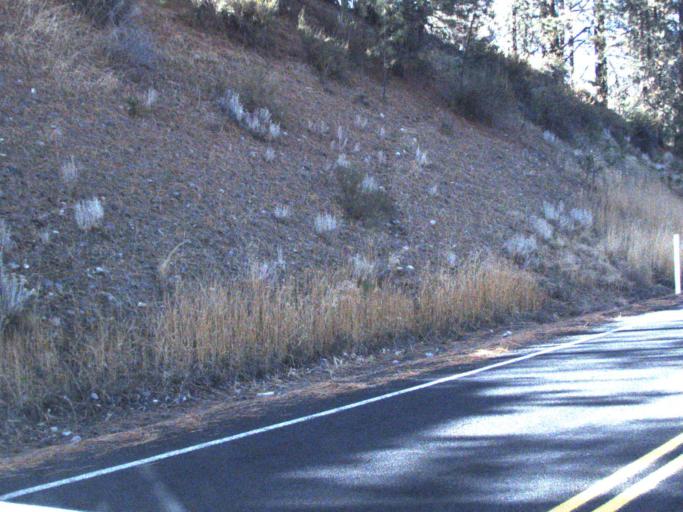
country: US
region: Washington
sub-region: Lincoln County
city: Davenport
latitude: 47.9069
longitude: -118.3066
